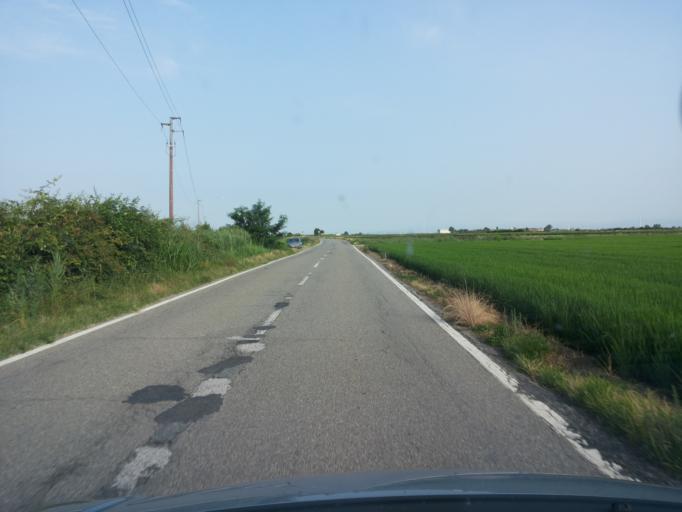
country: IT
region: Piedmont
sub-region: Provincia di Vercelli
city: Pezzana
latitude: 45.2601
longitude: 8.4585
